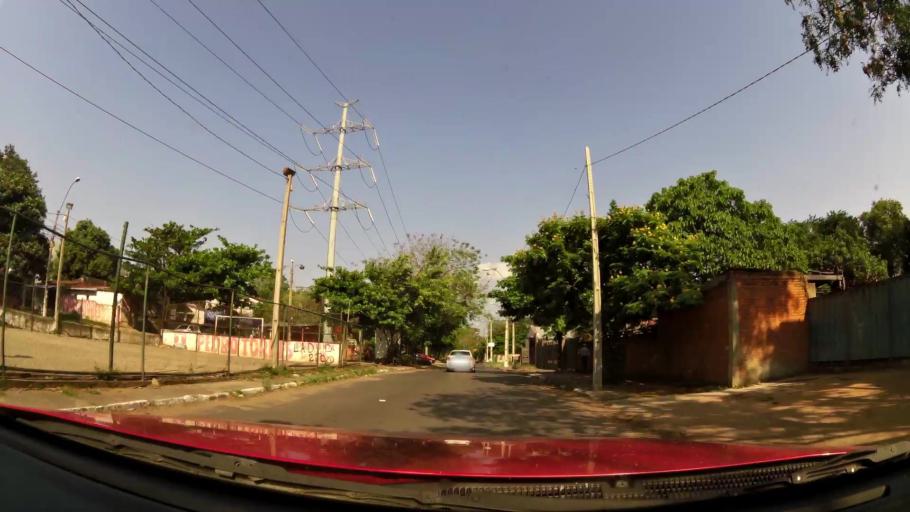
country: PY
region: Asuncion
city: Asuncion
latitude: -25.3122
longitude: -57.6356
